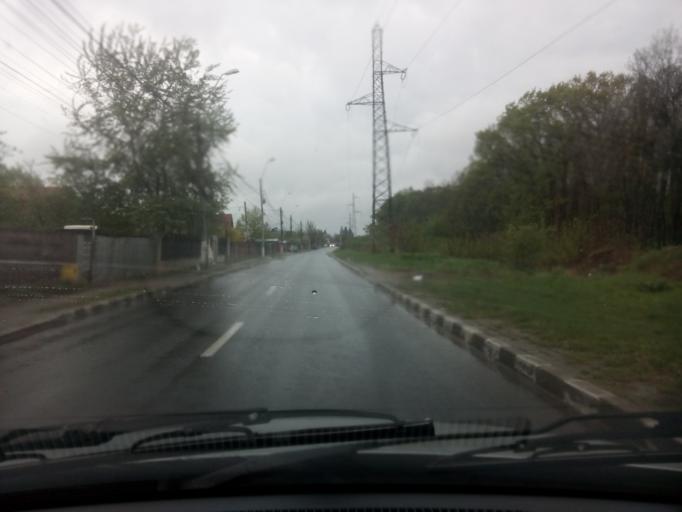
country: RO
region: Ilfov
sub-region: Voluntari City
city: Voluntari
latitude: 44.4879
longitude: 26.1607
